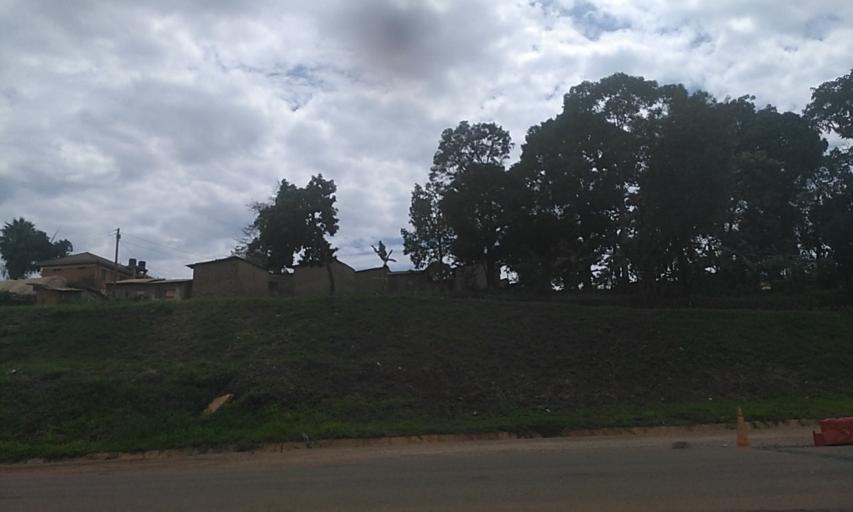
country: UG
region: Central Region
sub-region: Wakiso District
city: Kireka
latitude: 0.3663
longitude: 32.6117
